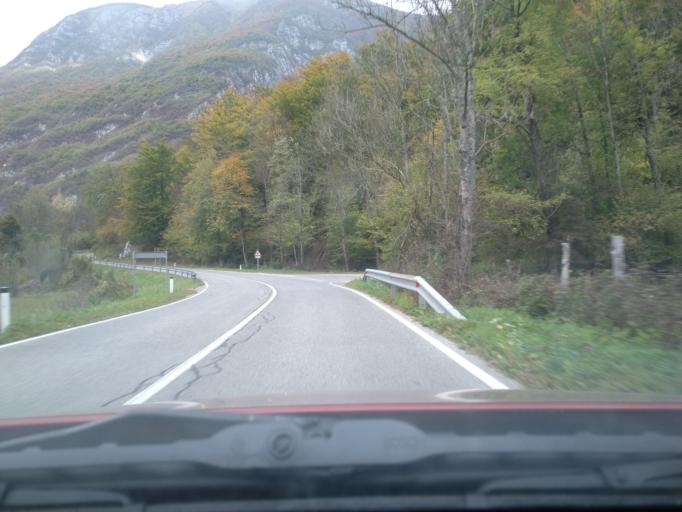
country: SI
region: Bovec
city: Bovec
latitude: 46.2838
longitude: 13.5231
